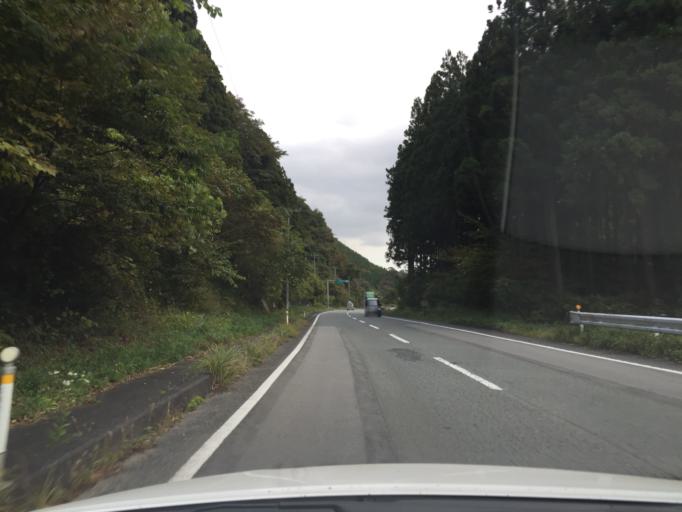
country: JP
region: Ibaraki
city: Kitaibaraki
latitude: 36.9391
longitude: 140.6658
